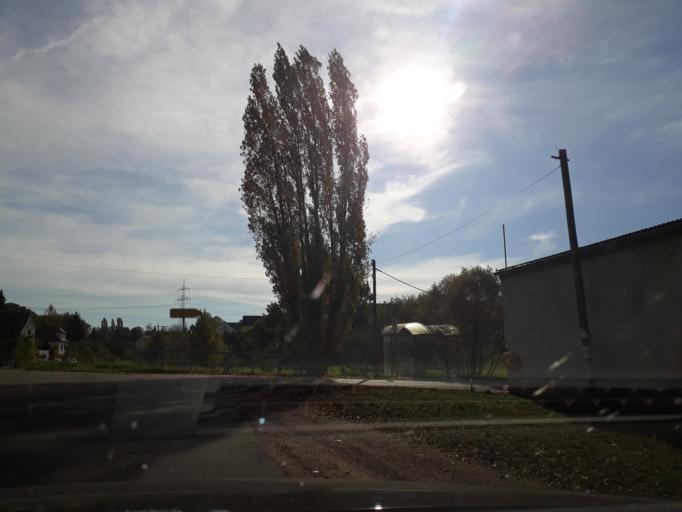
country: DE
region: Saxony
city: Niederstriegis
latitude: 51.1107
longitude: 13.1596
